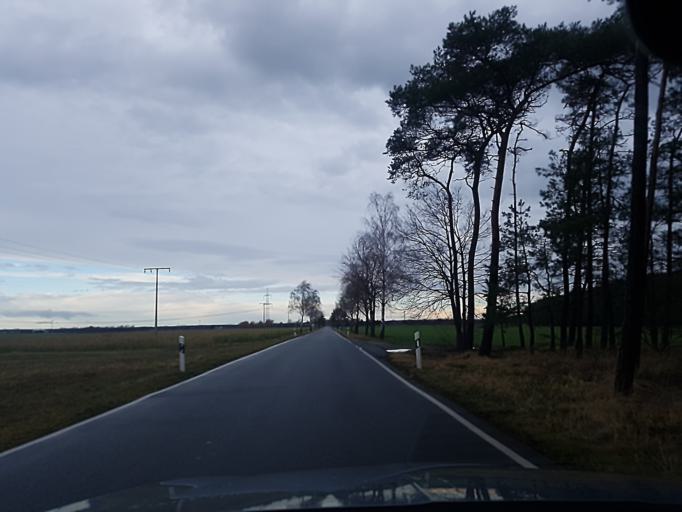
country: DE
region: Brandenburg
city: Schilda
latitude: 51.6116
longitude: 13.3778
